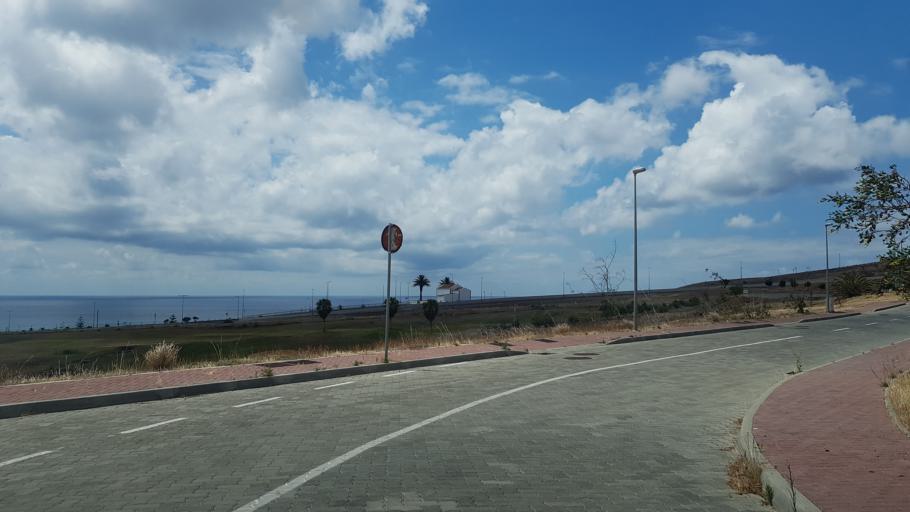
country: PT
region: Madeira
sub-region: Porto Santo
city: Vila de Porto Santo
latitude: 33.0481
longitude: -16.3629
